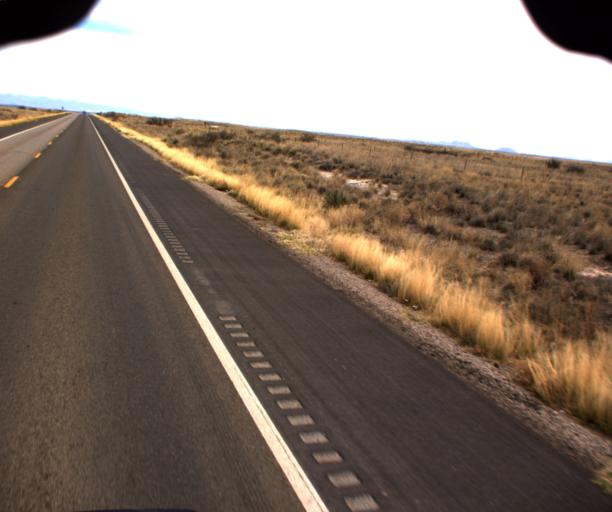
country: US
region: Arizona
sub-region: Cochise County
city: Willcox
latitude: 32.2326
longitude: -109.8038
